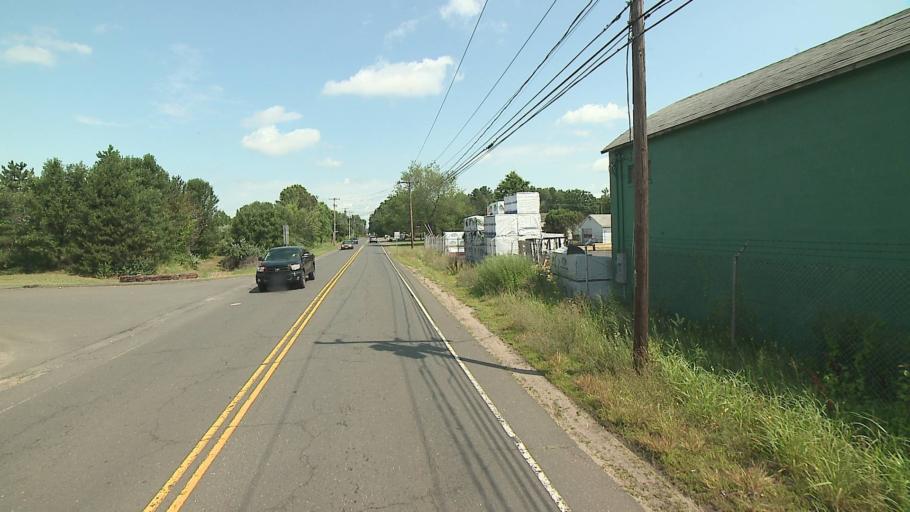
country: US
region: Connecticut
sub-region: Hartford County
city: Plainville
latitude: 41.6513
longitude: -72.8749
